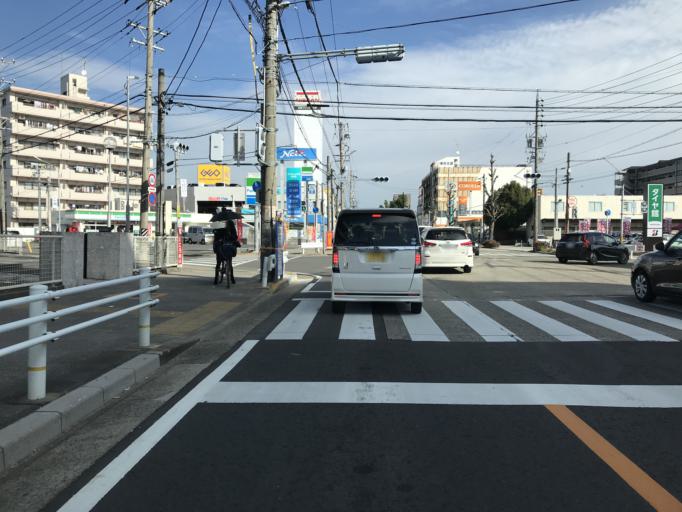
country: JP
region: Aichi
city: Nagoya-shi
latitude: 35.2004
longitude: 136.9191
